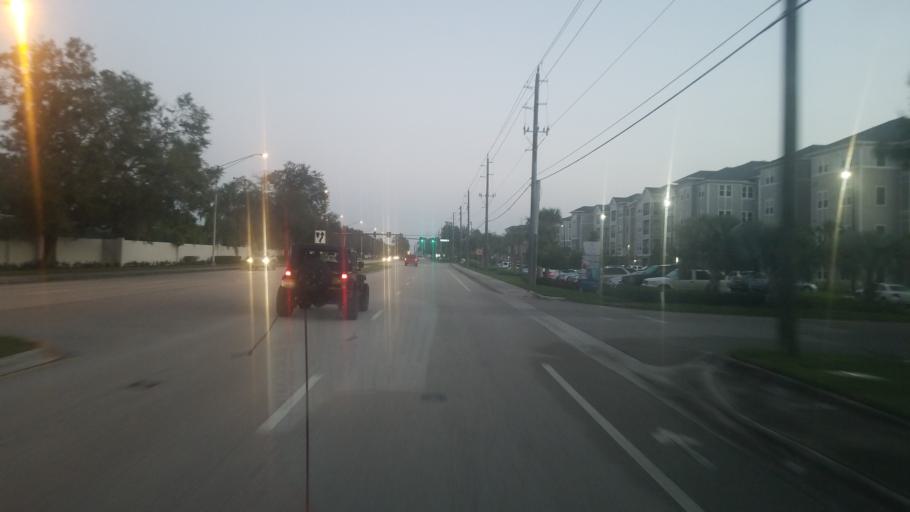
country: US
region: Florida
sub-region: Sarasota County
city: Fruitville
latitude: 27.3102
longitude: -82.4514
